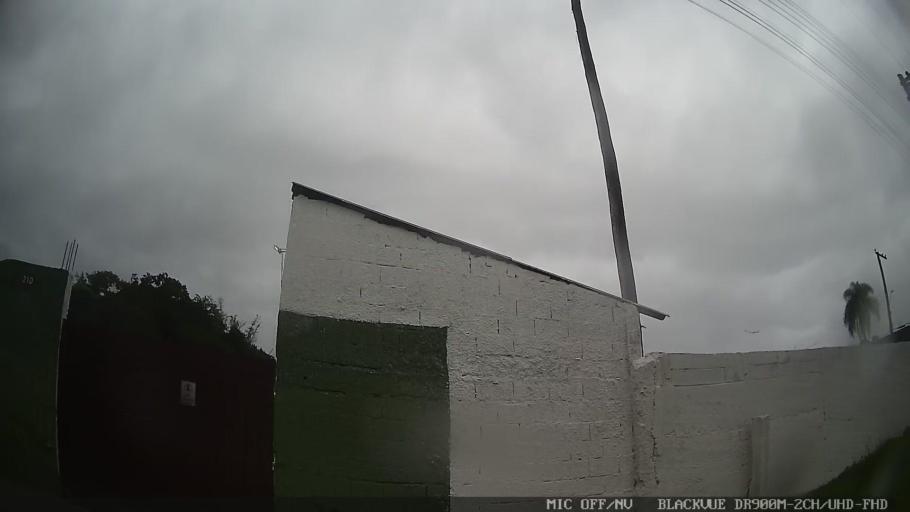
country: BR
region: Sao Paulo
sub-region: Itanhaem
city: Itanhaem
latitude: -24.1748
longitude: -46.8264
